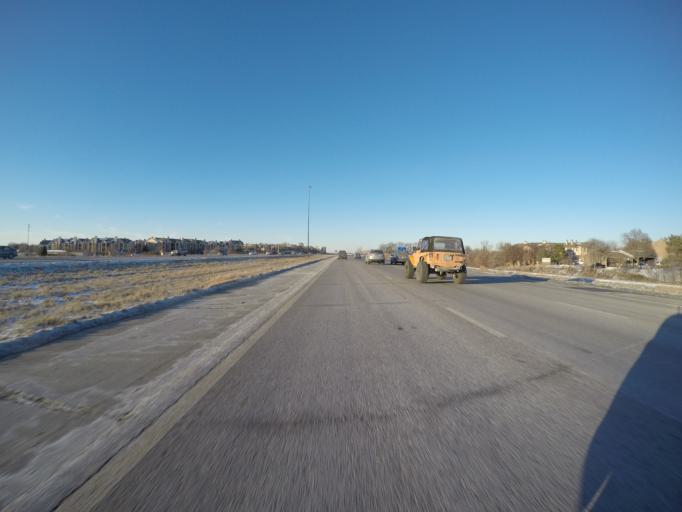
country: US
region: Kansas
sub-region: Johnson County
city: Lenexa
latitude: 38.9604
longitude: -94.7754
